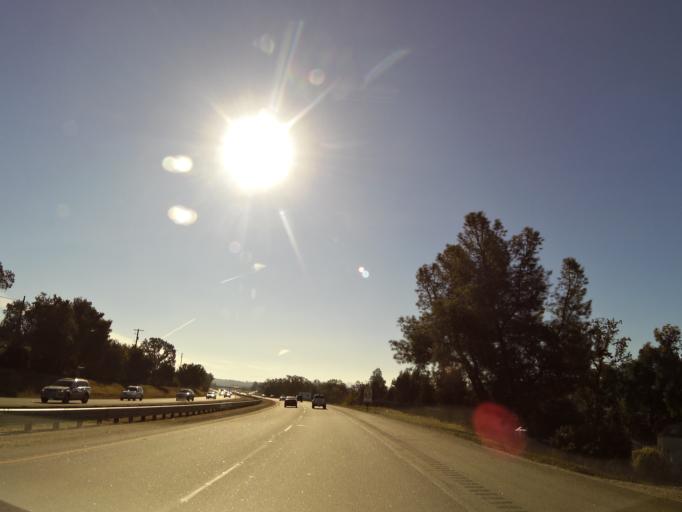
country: US
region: California
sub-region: San Luis Obispo County
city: Templeton
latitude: 35.5200
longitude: -120.7039
